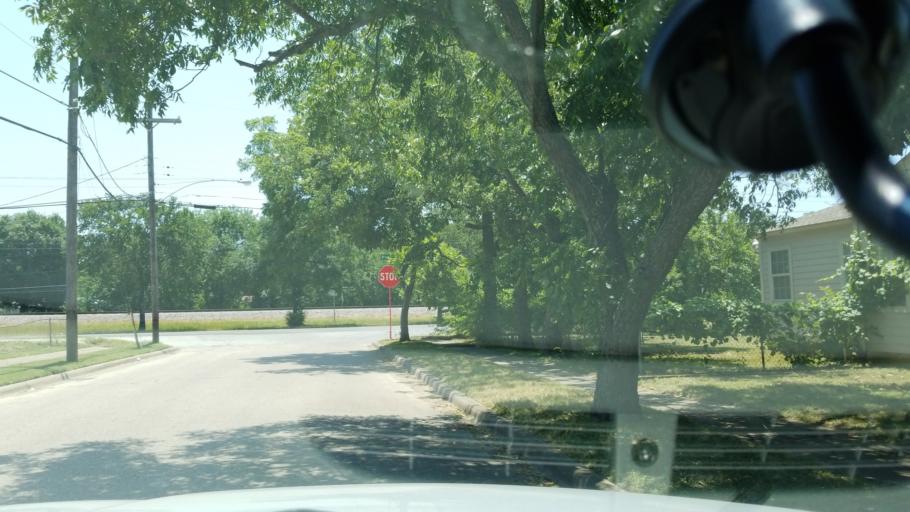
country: US
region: Texas
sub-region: Dallas County
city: Cockrell Hill
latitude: 32.7232
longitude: -96.8637
